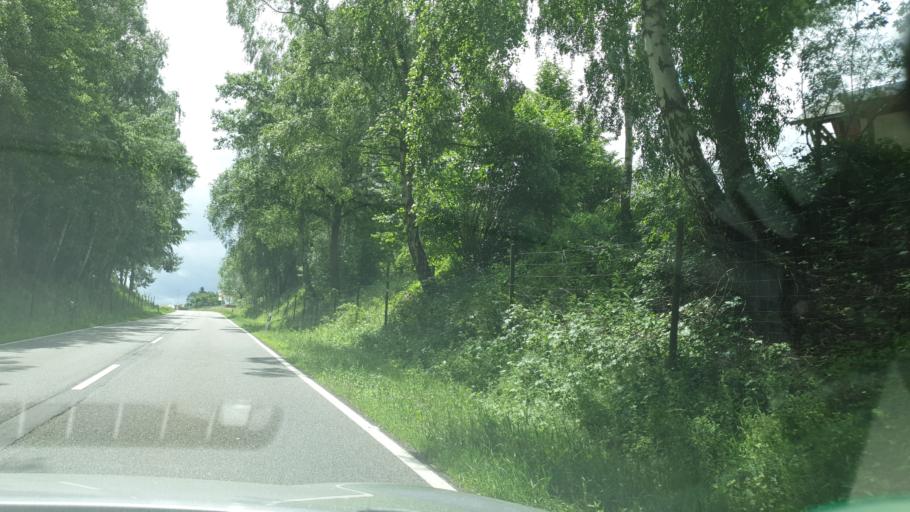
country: DE
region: Rheinland-Pfalz
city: Hillscheid
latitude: 50.4161
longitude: 7.6896
